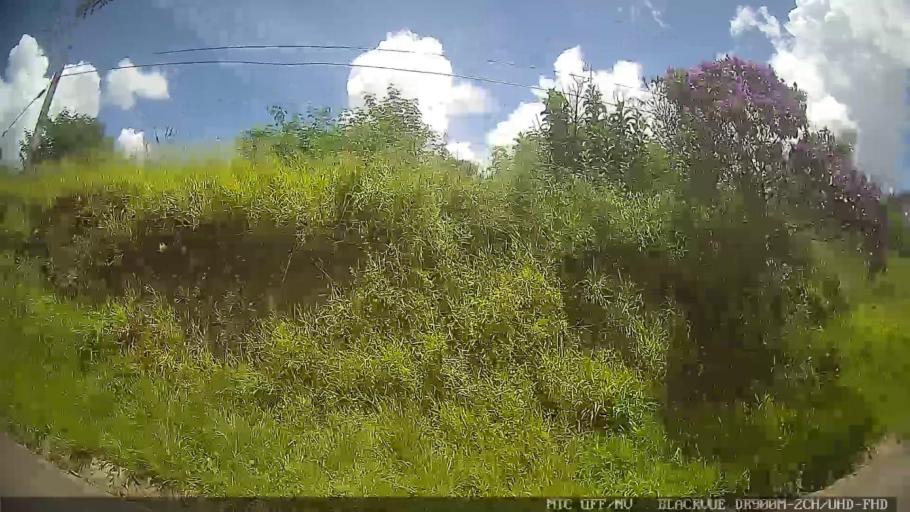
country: BR
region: Sao Paulo
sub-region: Braganca Paulista
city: Braganca Paulista
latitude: -22.8763
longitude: -46.6104
